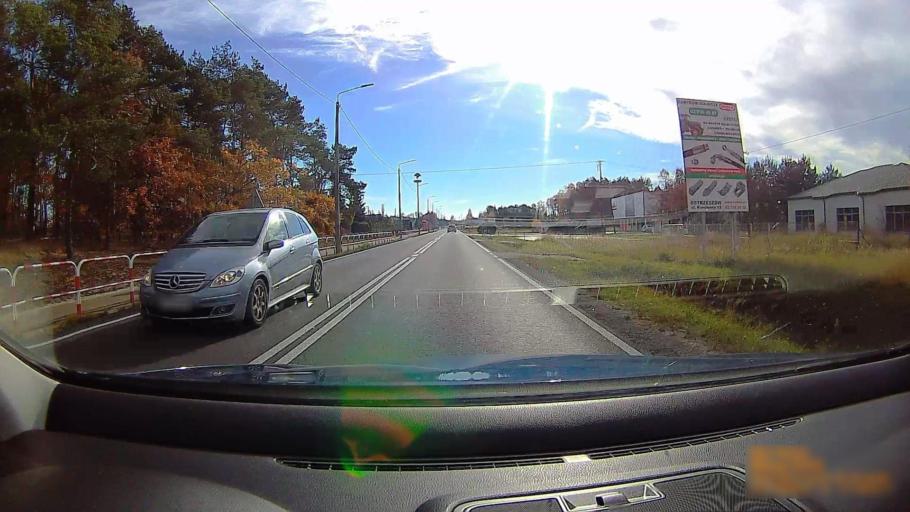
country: PL
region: Greater Poland Voivodeship
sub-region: Powiat ostrzeszowski
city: Ostrzeszow
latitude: 51.4466
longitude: 17.9106
